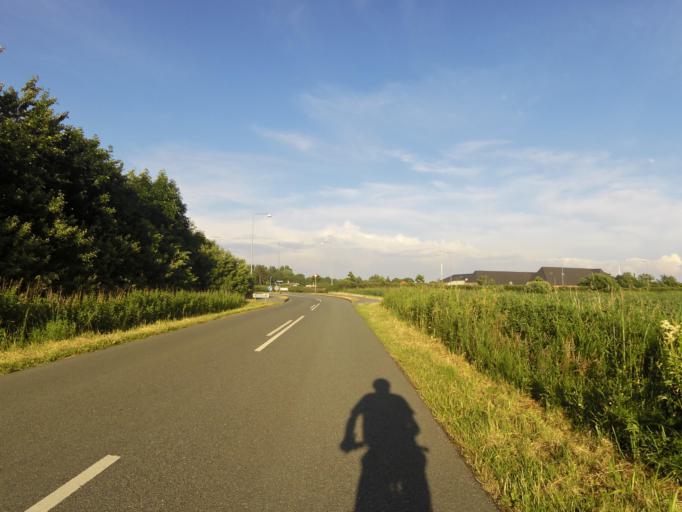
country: DK
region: South Denmark
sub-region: Tonder Kommune
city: Sherrebek
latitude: 55.1651
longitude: 8.7557
